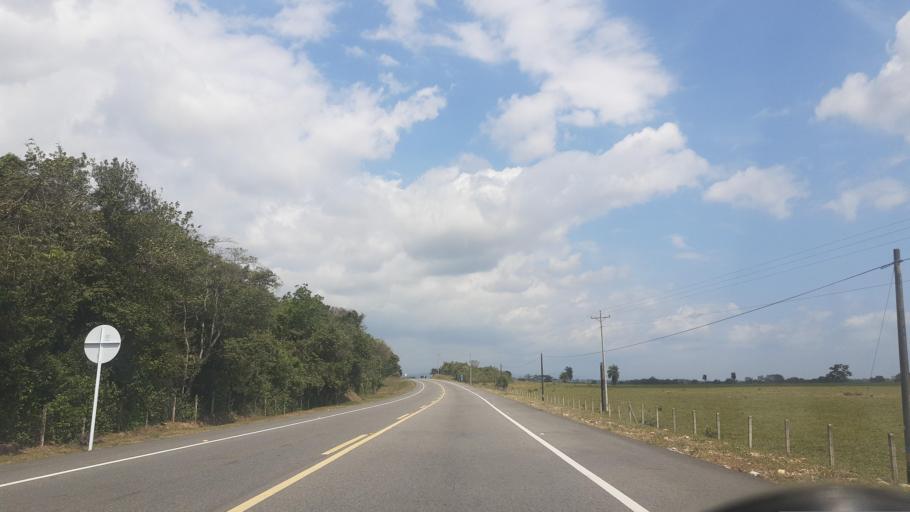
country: CO
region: Casanare
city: Tauramena
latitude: 4.9023
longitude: -72.6763
